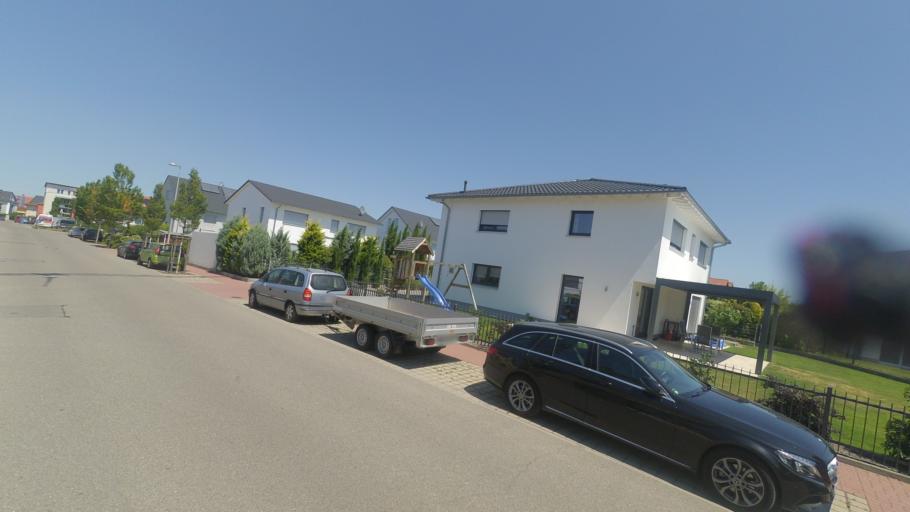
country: DE
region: Rheinland-Pfalz
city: Limburgerhof
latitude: 49.4261
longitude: 8.3985
